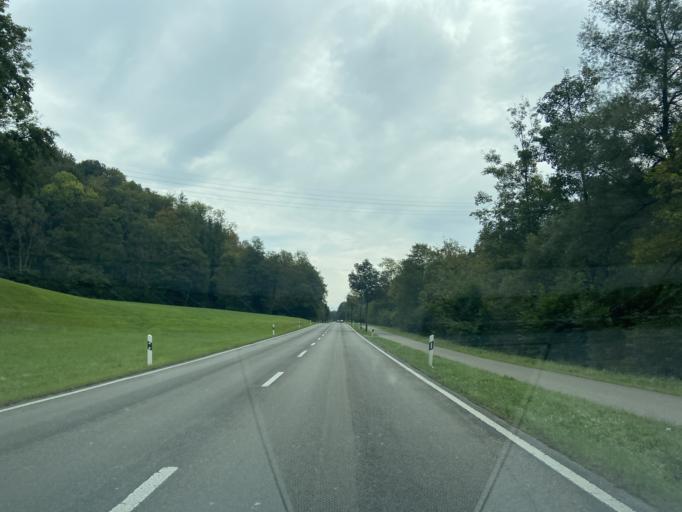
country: CH
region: Zurich
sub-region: Bezirk Pfaeffikon
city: Effretikon / Watt
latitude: 47.4290
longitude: 8.7077
